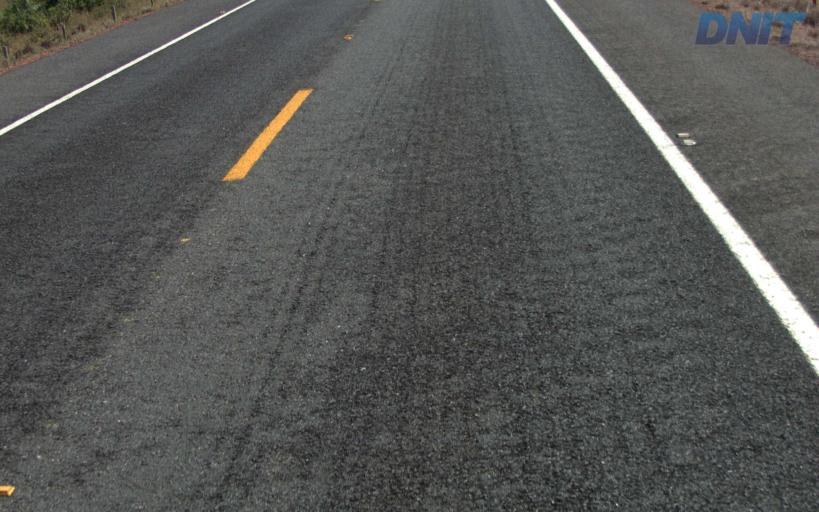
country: BR
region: Goias
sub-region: Sao Miguel Do Araguaia
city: Sao Miguel do Araguaia
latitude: -13.2884
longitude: -50.4441
